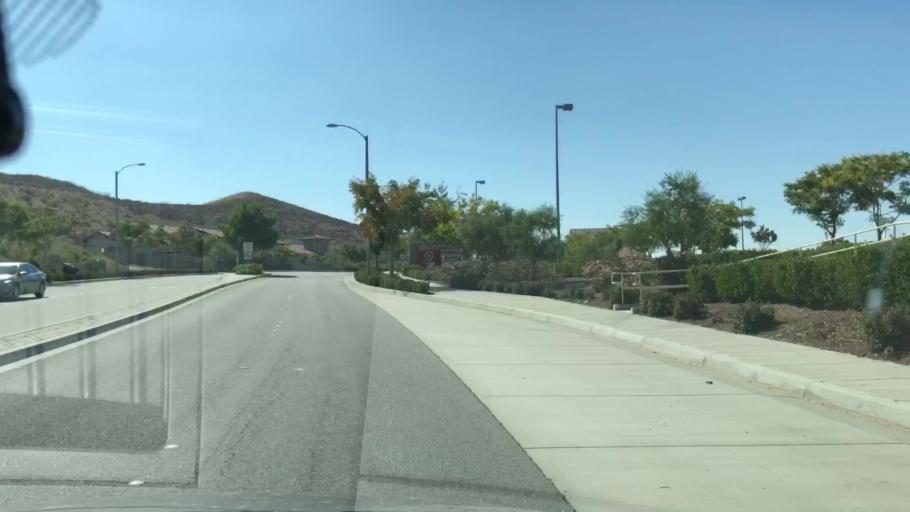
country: US
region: California
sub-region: Los Angeles County
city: Santa Clarita
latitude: 34.3936
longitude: -118.4636
